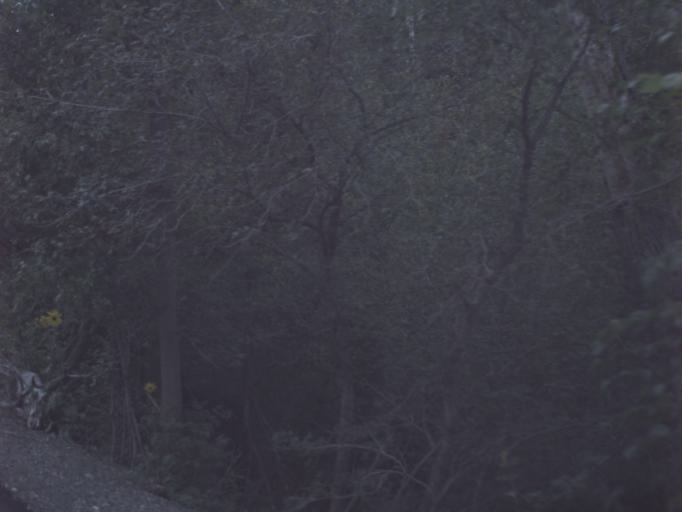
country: US
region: Utah
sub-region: Utah County
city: Cedar Hills
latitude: 40.4478
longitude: -111.6435
